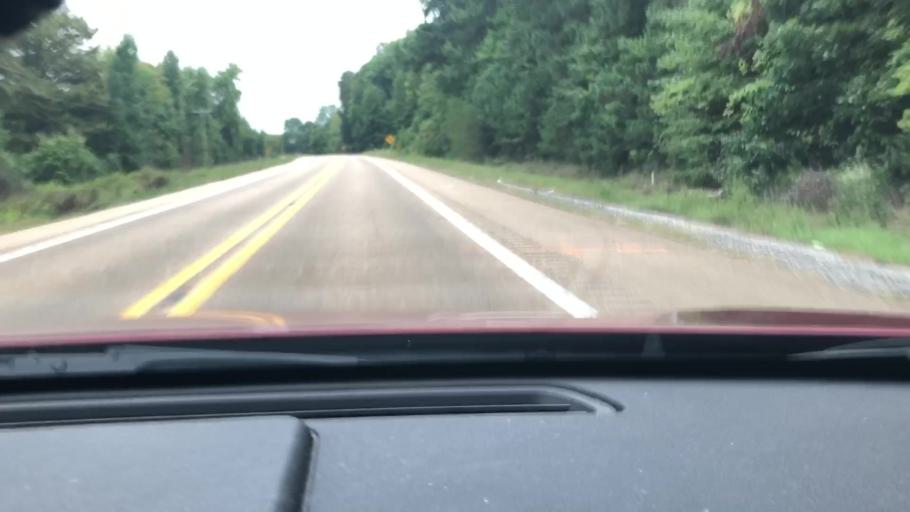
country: US
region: Arkansas
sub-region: Miller County
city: Texarkana
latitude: 33.4161
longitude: -93.8118
